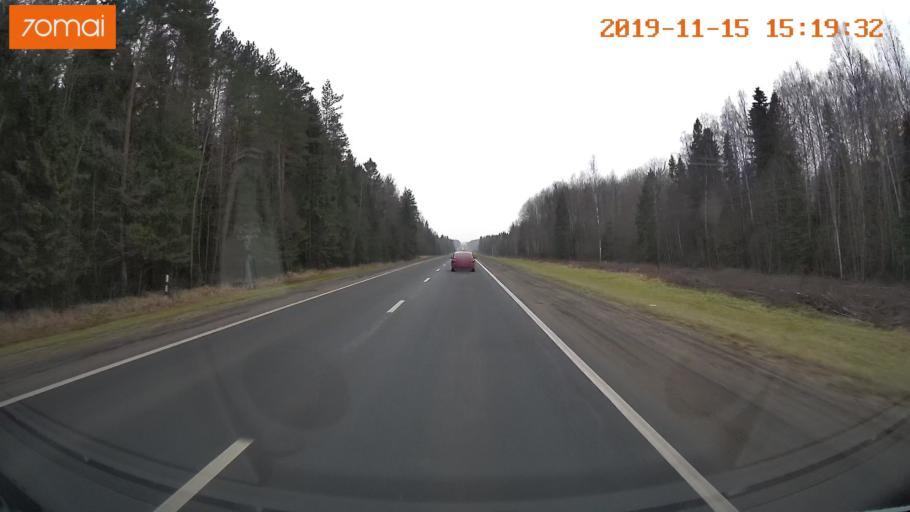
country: RU
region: Jaroslavl
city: Danilov
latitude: 58.2333
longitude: 40.1761
